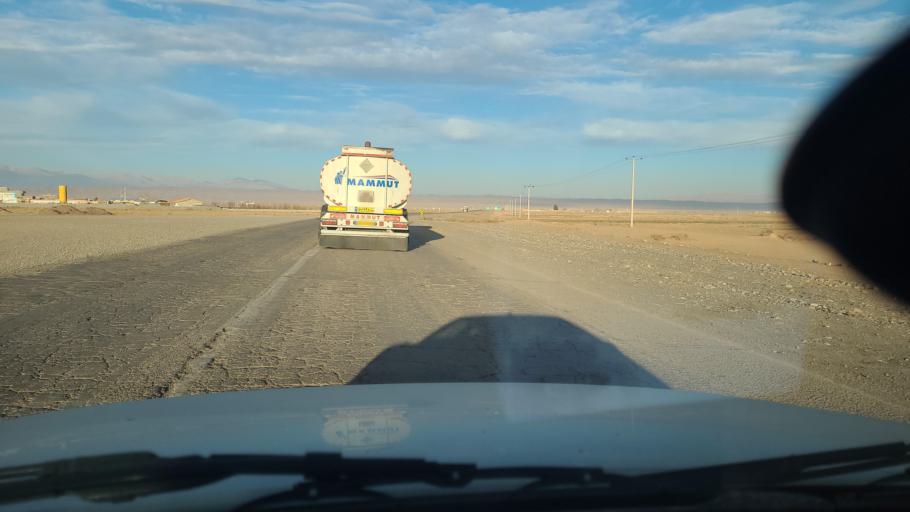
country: IR
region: Razavi Khorasan
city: Neqab
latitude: 36.6129
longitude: 57.5954
